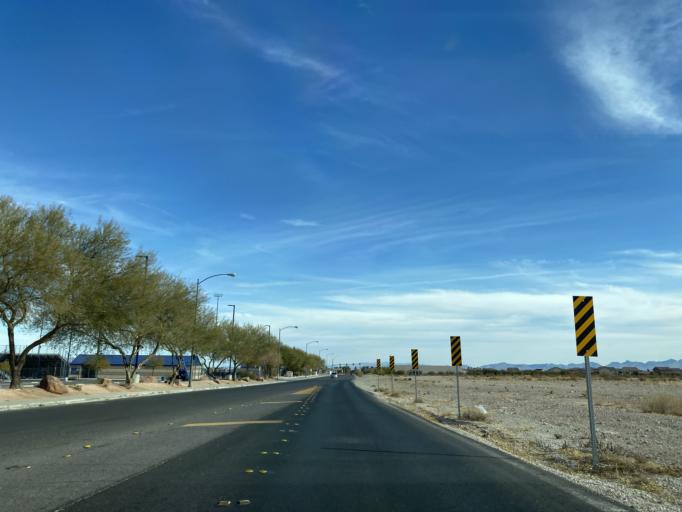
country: US
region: Nevada
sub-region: Clark County
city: Enterprise
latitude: 36.0482
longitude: -115.2687
